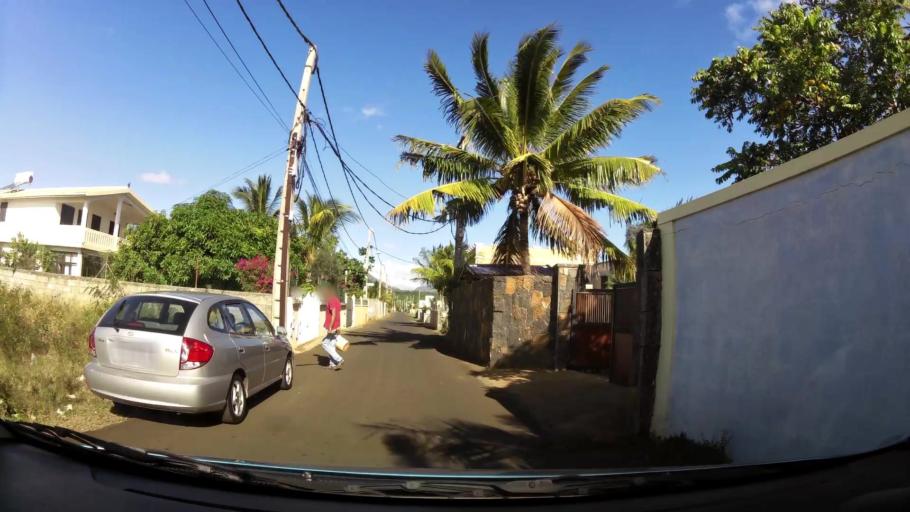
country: MU
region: Black River
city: Albion
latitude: -20.2019
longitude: 57.4109
